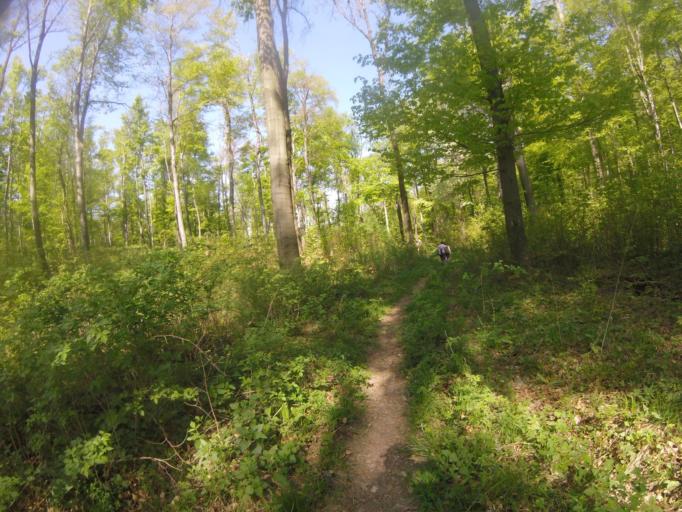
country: HU
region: Komarom-Esztergom
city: Piliscsev
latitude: 47.7053
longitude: 18.8527
